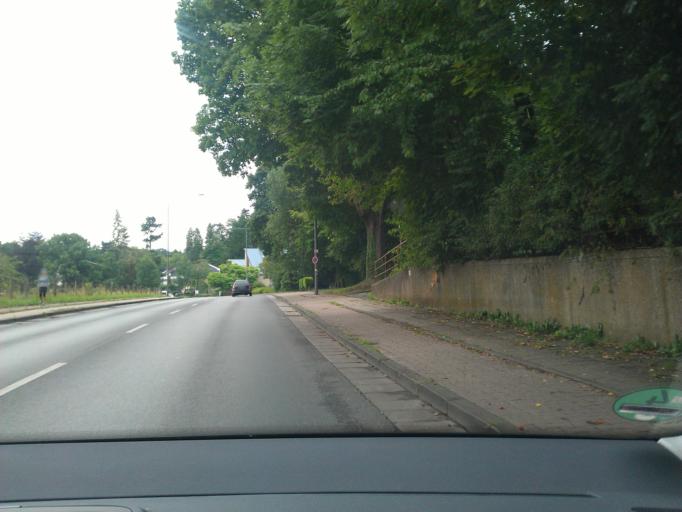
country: DE
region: North Rhine-Westphalia
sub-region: Regierungsbezirk Koln
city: Aachen
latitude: 50.7565
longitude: 6.0663
